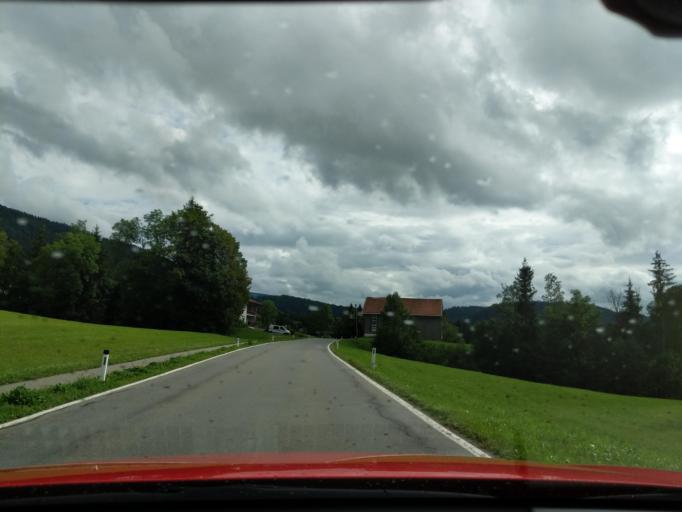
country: AT
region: Vorarlberg
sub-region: Politischer Bezirk Bregenz
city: Krumbach
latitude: 47.4966
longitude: 9.9463
